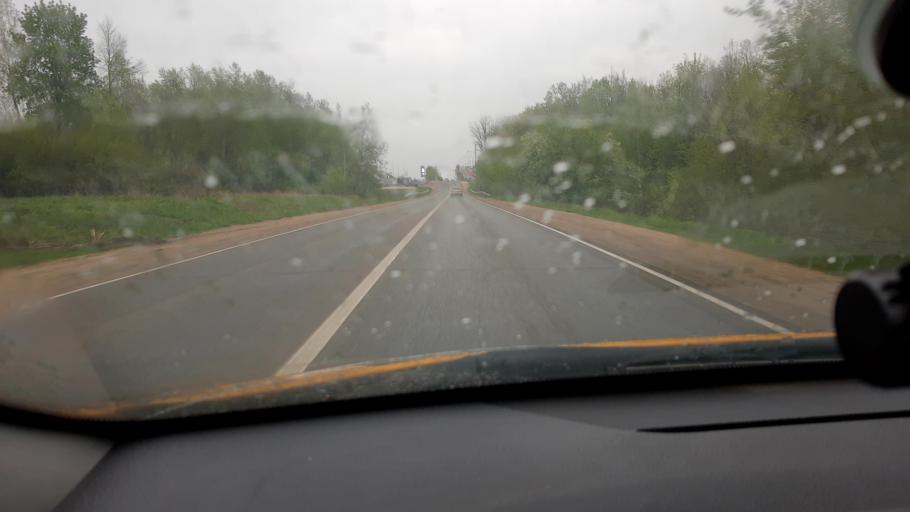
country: RU
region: Tula
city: Zaokskiy
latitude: 54.7518
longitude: 37.4385
